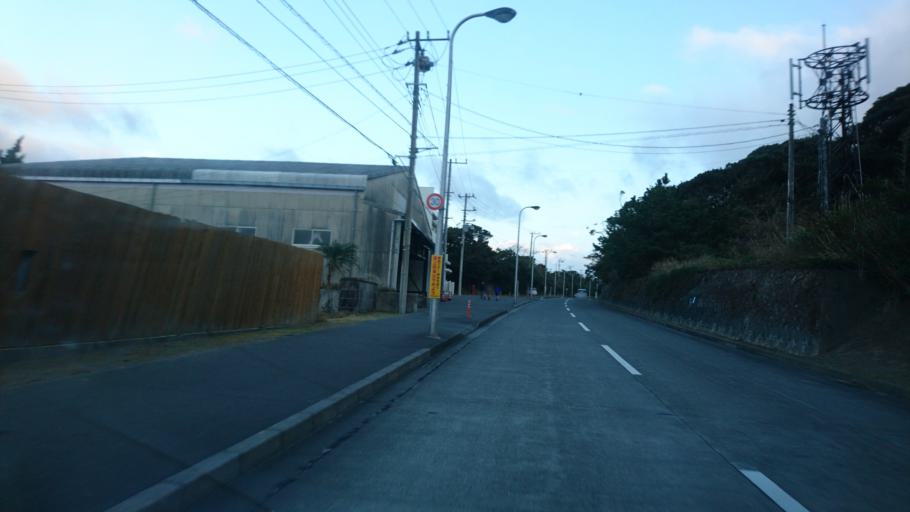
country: JP
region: Shizuoka
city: Shimoda
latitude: 34.3705
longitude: 139.2549
